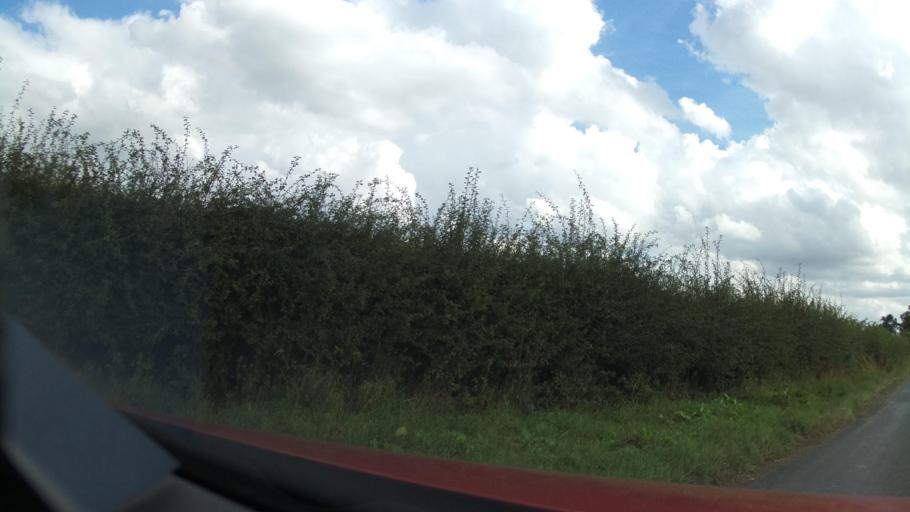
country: GB
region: England
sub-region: North Yorkshire
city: Bedale
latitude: 54.2266
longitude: -1.6415
